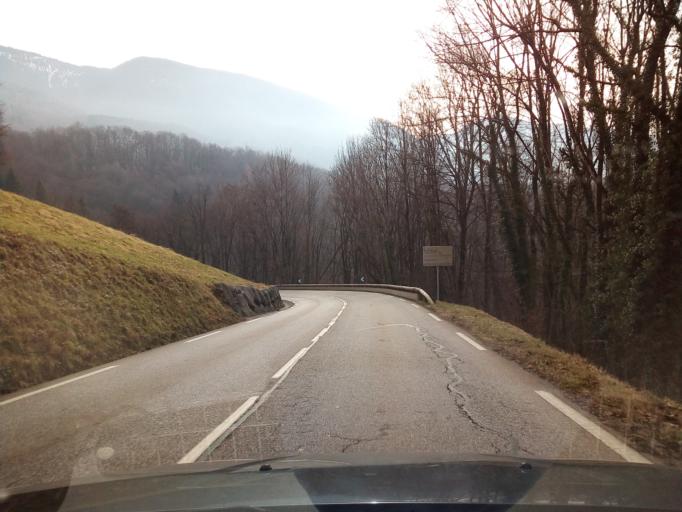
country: FR
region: Rhone-Alpes
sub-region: Departement de l'Isere
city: Vaulnaveys-le-Haut
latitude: 45.1424
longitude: 5.8331
